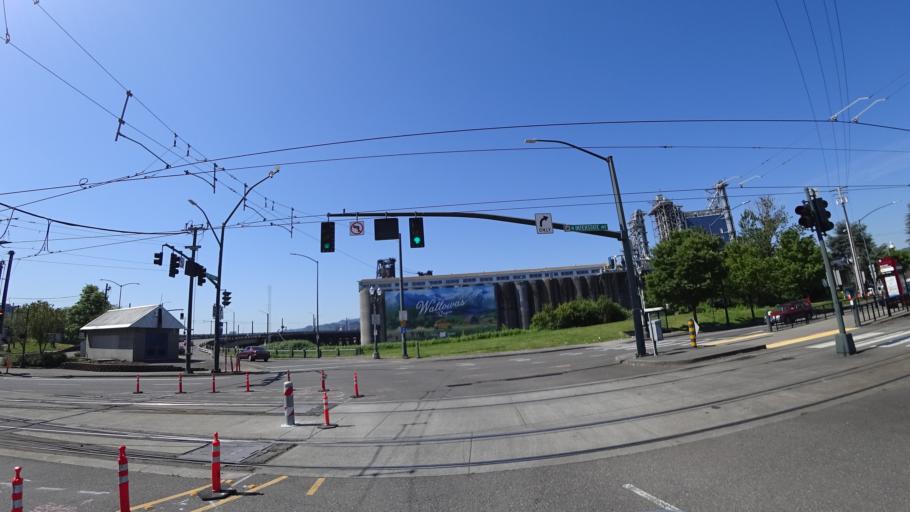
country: US
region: Oregon
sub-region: Multnomah County
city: Portland
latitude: 45.5300
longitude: -122.6672
